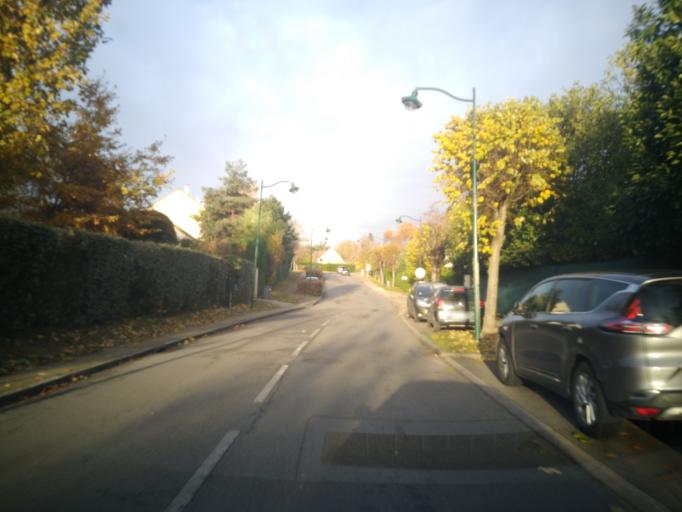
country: FR
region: Ile-de-France
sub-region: Departement des Yvelines
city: Fourqueux
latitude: 48.8839
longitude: 2.0673
